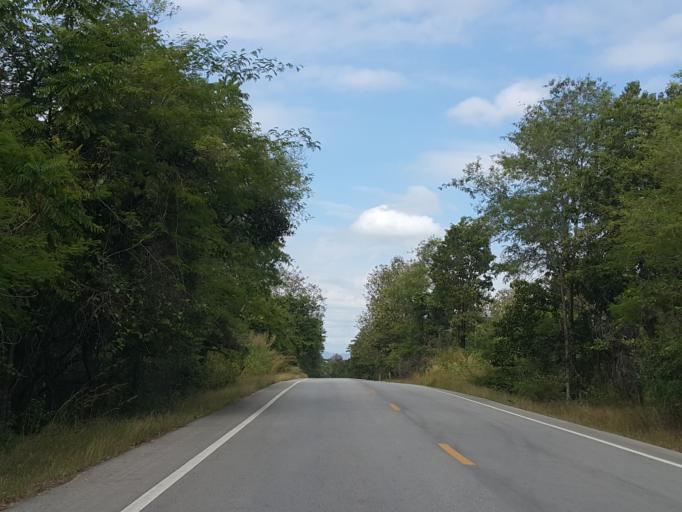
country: TH
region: Lampang
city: Lampang
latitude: 18.4123
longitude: 99.4511
